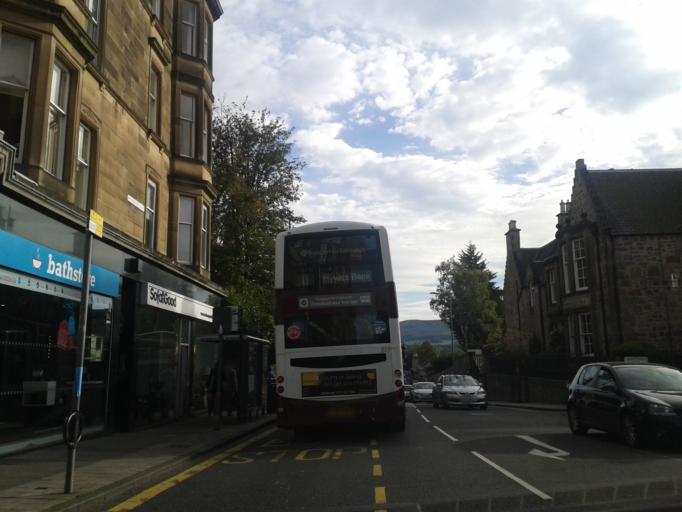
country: GB
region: Scotland
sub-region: Edinburgh
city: Edinburgh
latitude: 55.9319
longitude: -3.2099
